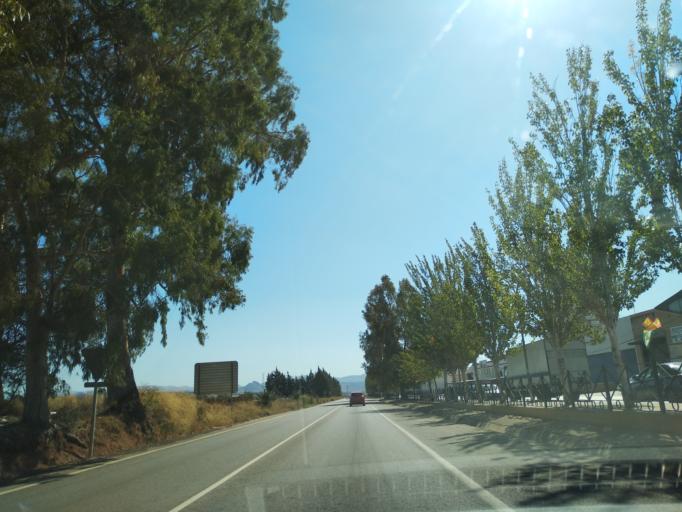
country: ES
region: Andalusia
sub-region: Provincia de Malaga
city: Mollina
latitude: 37.1170
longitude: -4.6547
